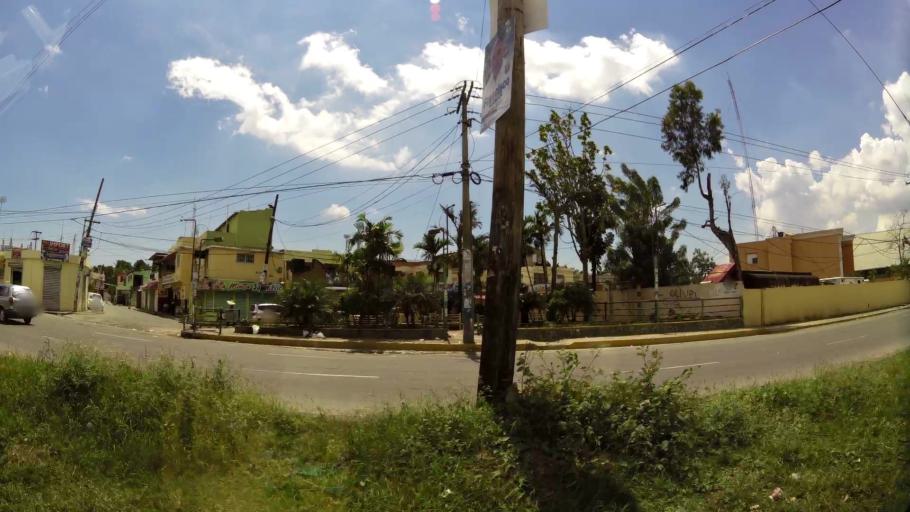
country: DO
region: Nacional
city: Ensanche Luperon
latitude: 18.5453
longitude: -69.8658
